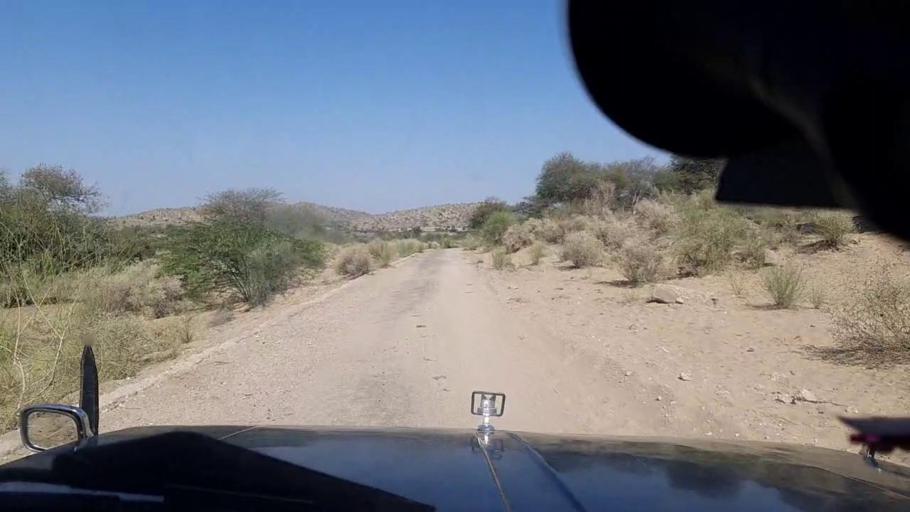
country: PK
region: Sindh
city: Diplo
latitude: 24.4195
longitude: 69.6604
